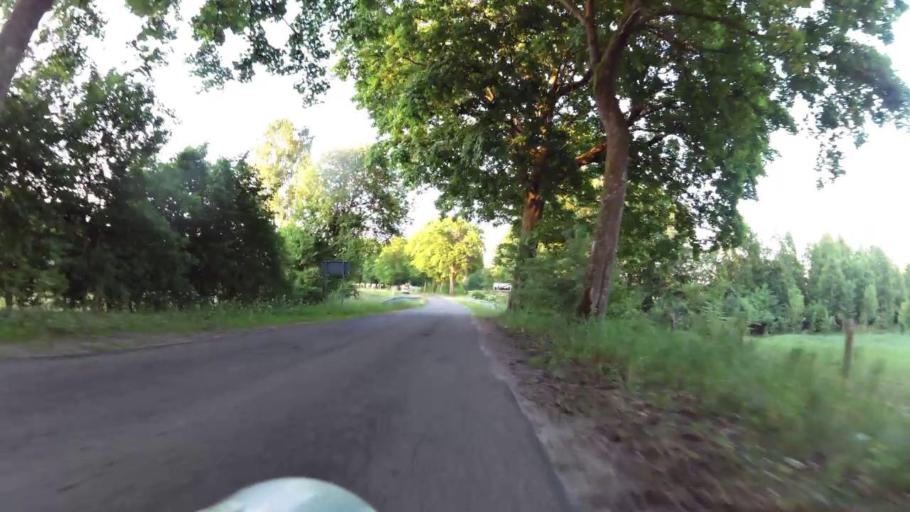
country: PL
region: West Pomeranian Voivodeship
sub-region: Powiat szczecinecki
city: Bialy Bor
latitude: 53.8622
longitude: 16.7557
